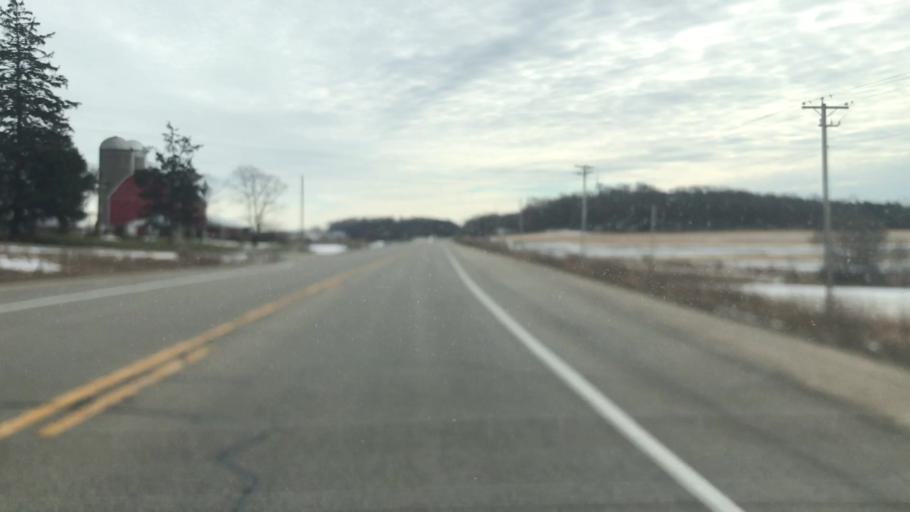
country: US
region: Wisconsin
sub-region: Dodge County
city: Mayville
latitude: 43.4425
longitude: -88.4912
